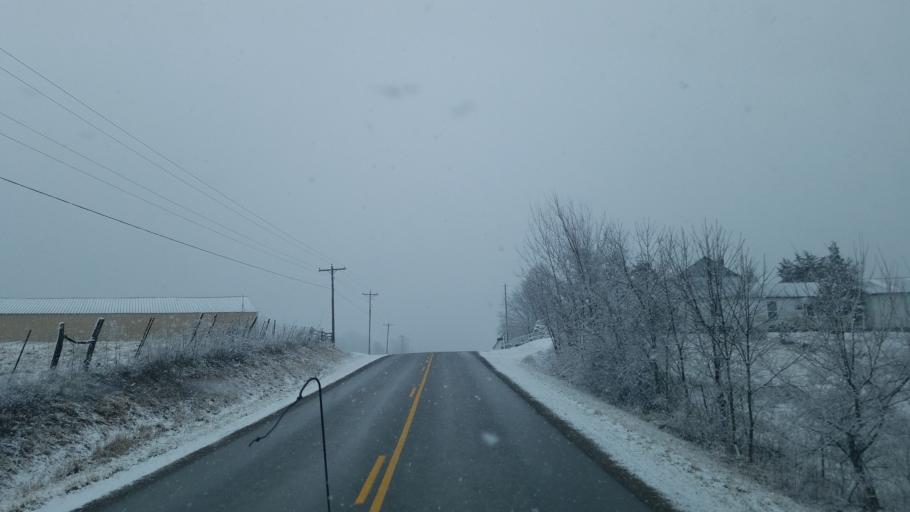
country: US
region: Ohio
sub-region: Champaign County
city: North Lewisburg
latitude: 40.3372
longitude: -83.6032
